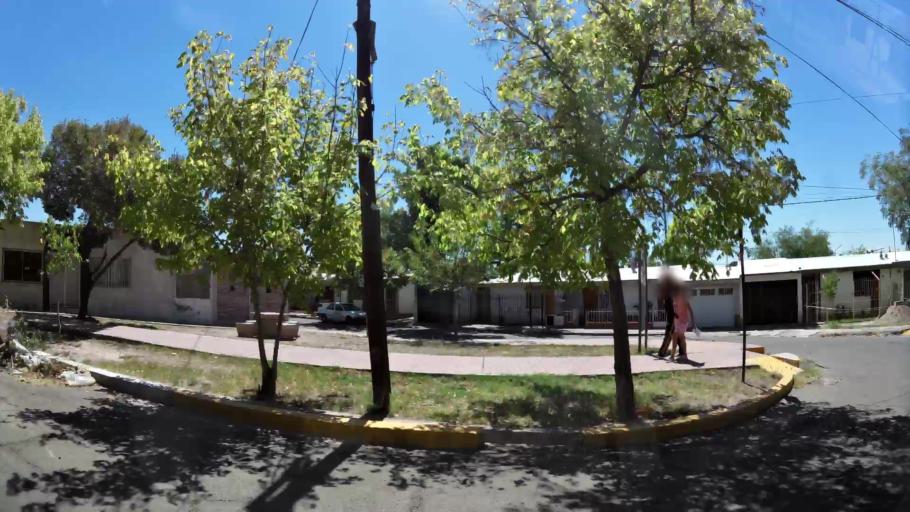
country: AR
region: Mendoza
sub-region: Departamento de Godoy Cruz
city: Godoy Cruz
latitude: -32.9371
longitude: -68.8741
